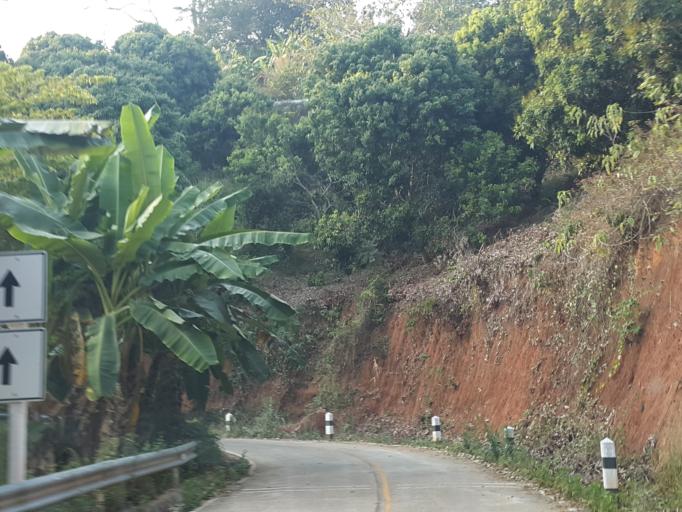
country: TH
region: Chiang Mai
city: Mae Taeng
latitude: 19.0761
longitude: 98.7681
